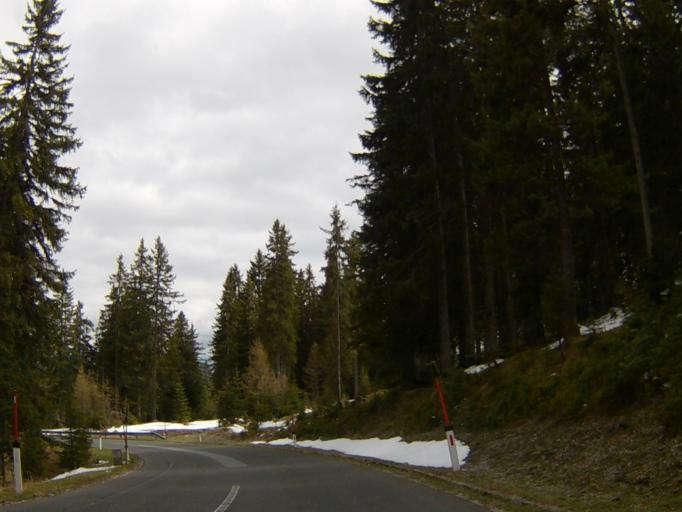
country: AT
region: Carinthia
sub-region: Politischer Bezirk Villach Land
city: Arnoldstein
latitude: 46.5909
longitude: 13.7217
